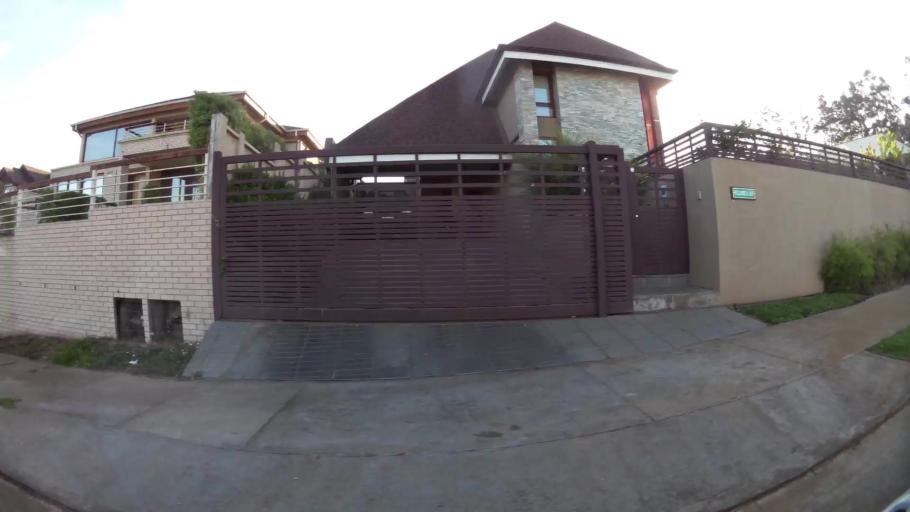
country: CL
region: Biobio
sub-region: Provincia de Concepcion
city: Concepcion
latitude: -36.8520
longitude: -73.0903
